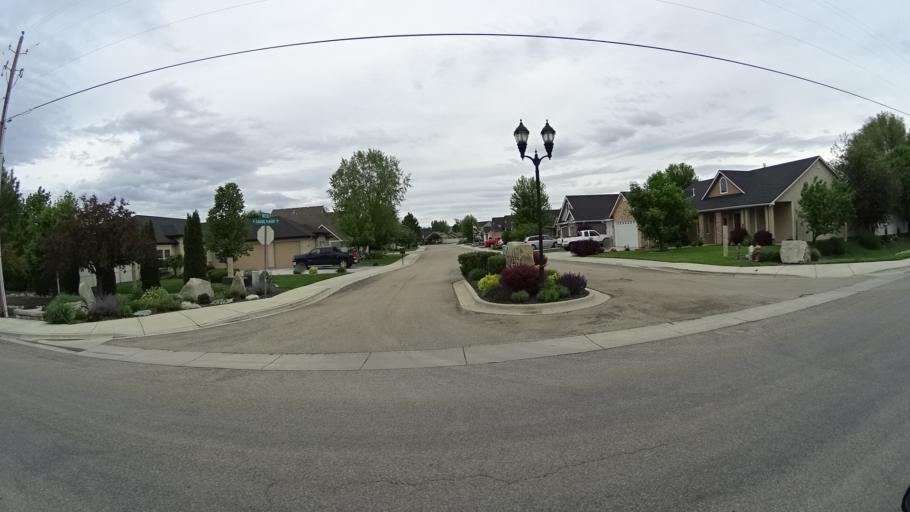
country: US
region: Idaho
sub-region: Ada County
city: Star
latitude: 43.7066
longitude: -116.4942
